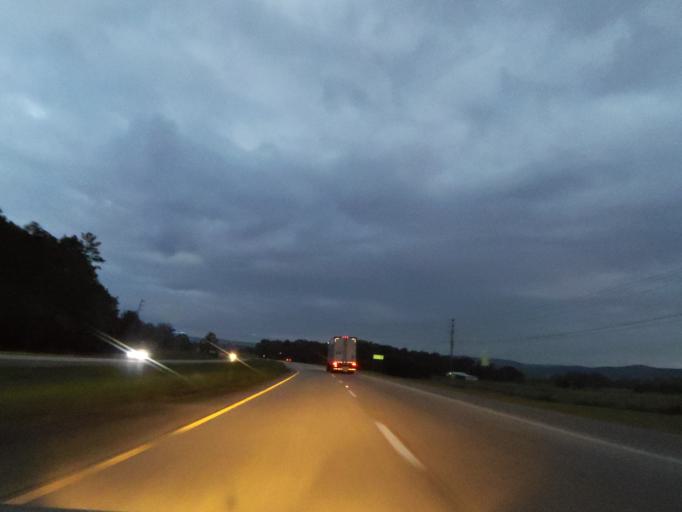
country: US
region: Alabama
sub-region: Madison County
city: New Hope
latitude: 34.6068
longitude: -86.2645
